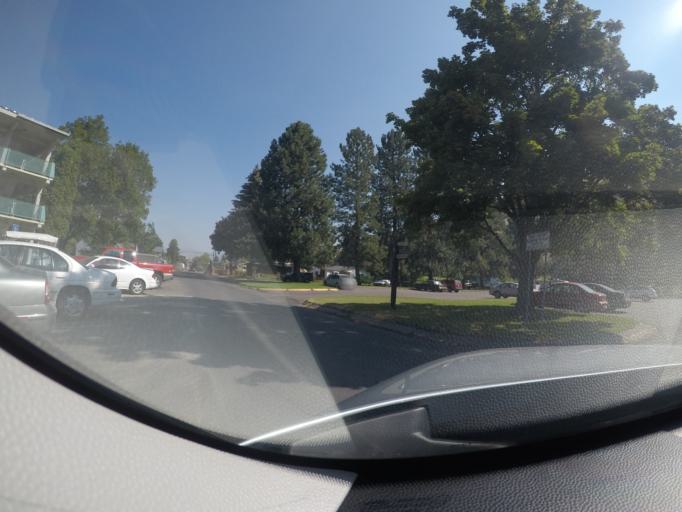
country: US
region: Montana
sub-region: Missoula County
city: Missoula
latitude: 46.8528
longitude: -113.9854
